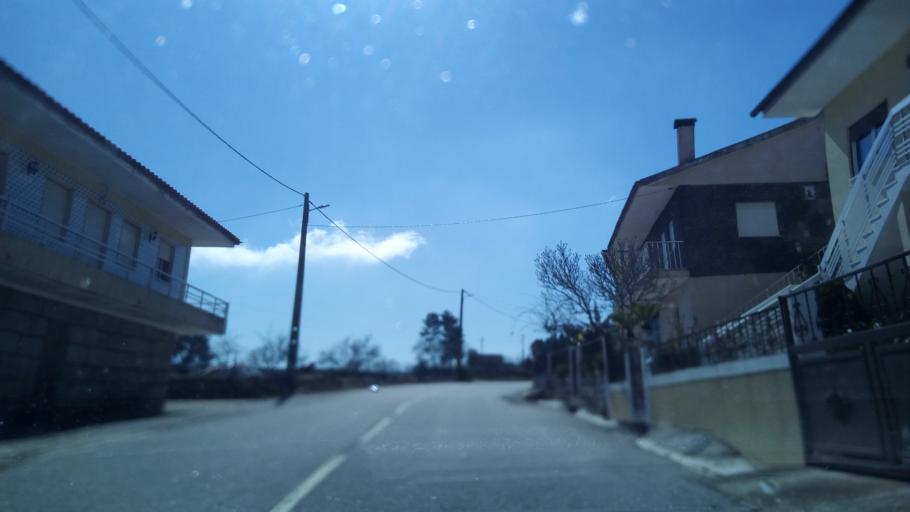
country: PT
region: Guarda
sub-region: Fornos de Algodres
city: Fornos de Algodres
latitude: 40.6475
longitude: -7.5322
